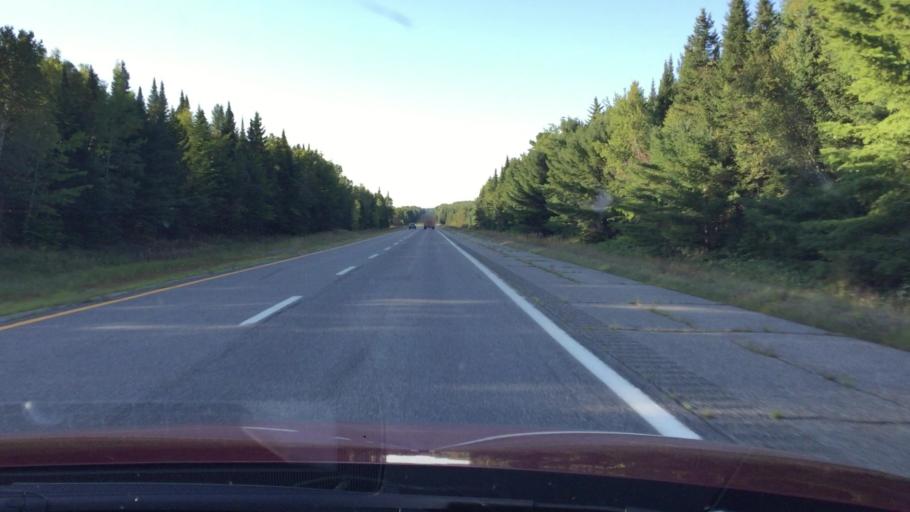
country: US
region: Maine
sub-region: Penobscot County
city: Patten
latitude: 45.8146
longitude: -68.4291
